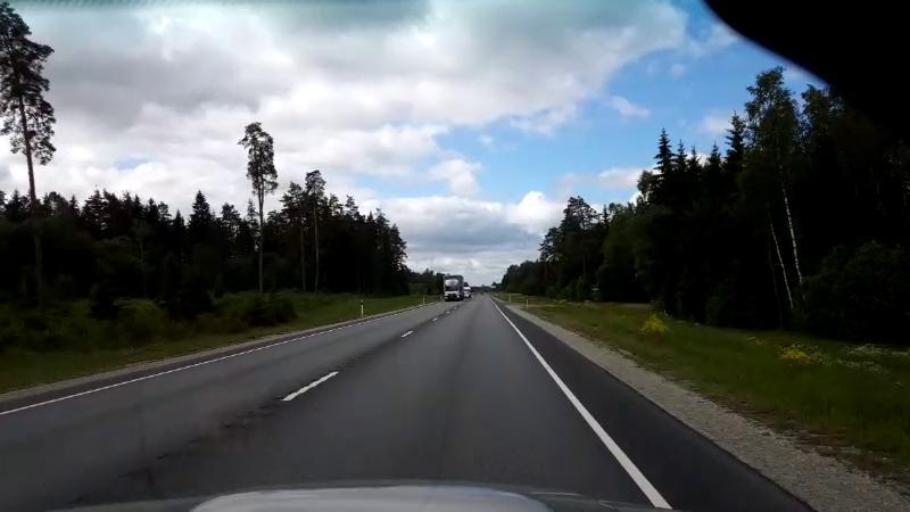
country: EE
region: Harju
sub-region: Nissi vald
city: Riisipere
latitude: 59.0911
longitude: 24.4637
